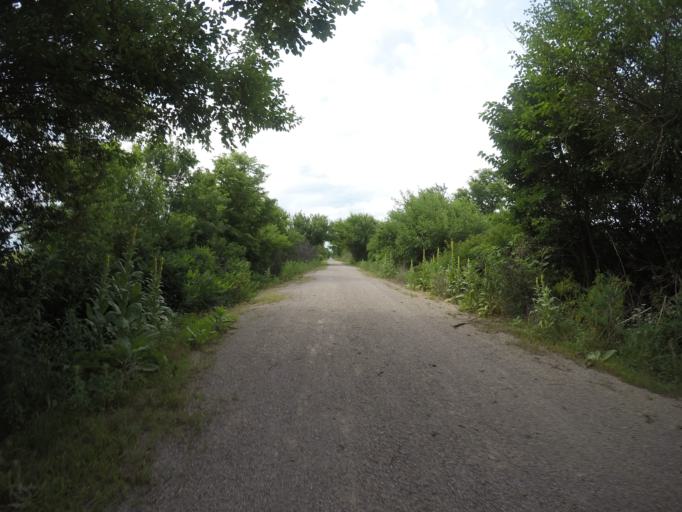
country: US
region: Kansas
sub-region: Anderson County
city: Garnett
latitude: 38.4303
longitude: -95.2635
